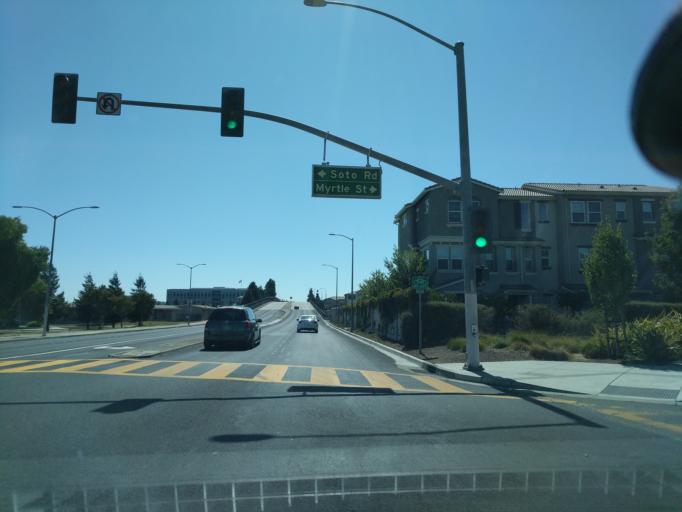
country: US
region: California
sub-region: Alameda County
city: Hayward
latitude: 37.6612
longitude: -122.0891
